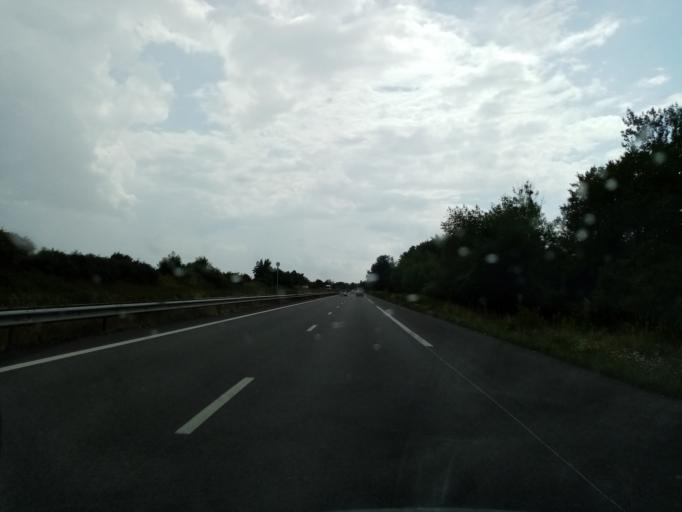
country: FR
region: Alsace
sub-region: Departement du Bas-Rhin
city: Herrlisheim
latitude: 48.7401
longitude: 7.9045
